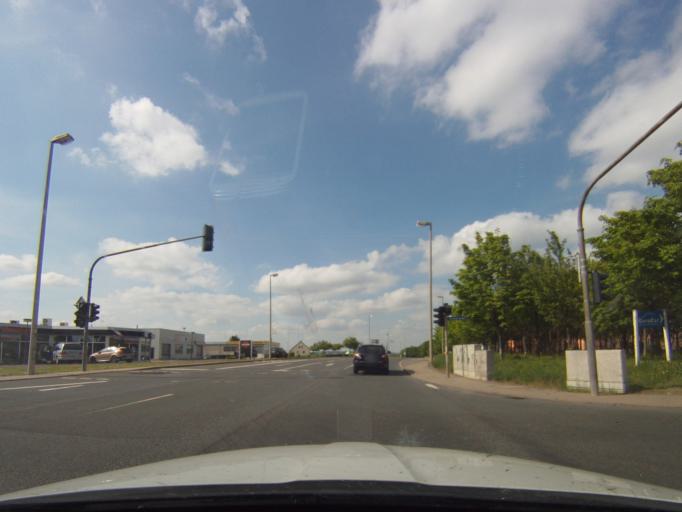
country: DE
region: Thuringia
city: Gera
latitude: 50.8755
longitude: 12.1166
